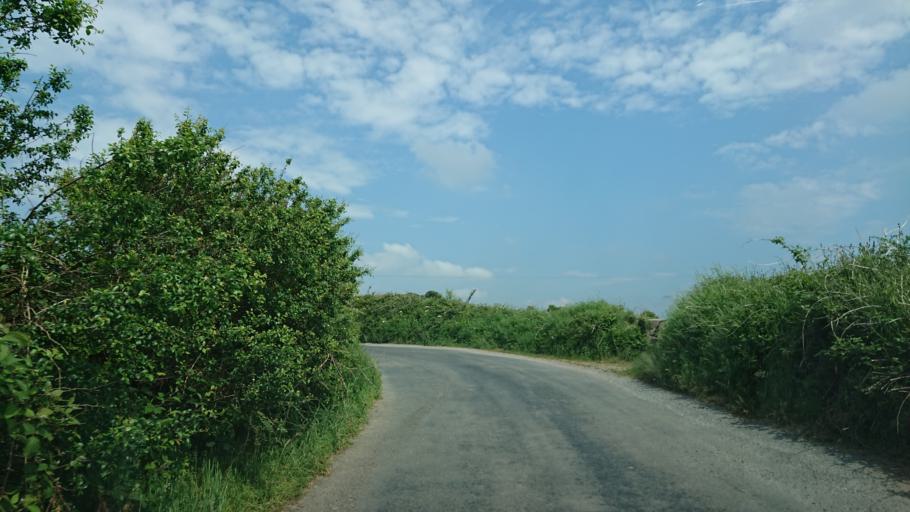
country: IE
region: Munster
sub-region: Waterford
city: Dunmore East
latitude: 52.2282
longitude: -7.0044
